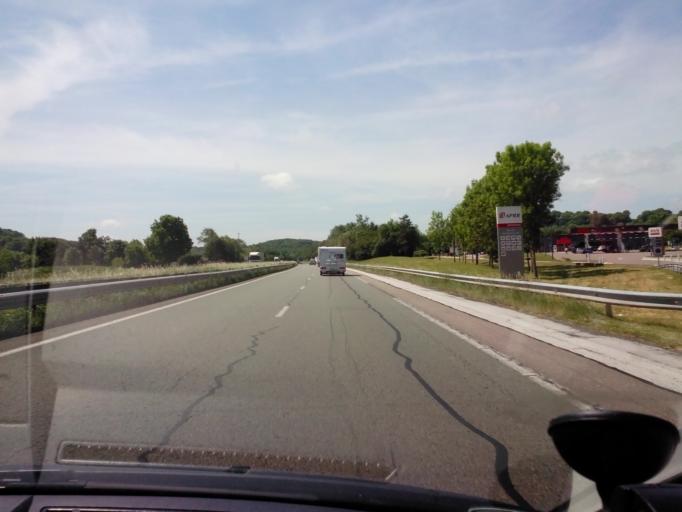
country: FR
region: Champagne-Ardenne
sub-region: Departement de la Haute-Marne
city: Avrecourt
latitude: 47.9783
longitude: 5.4999
